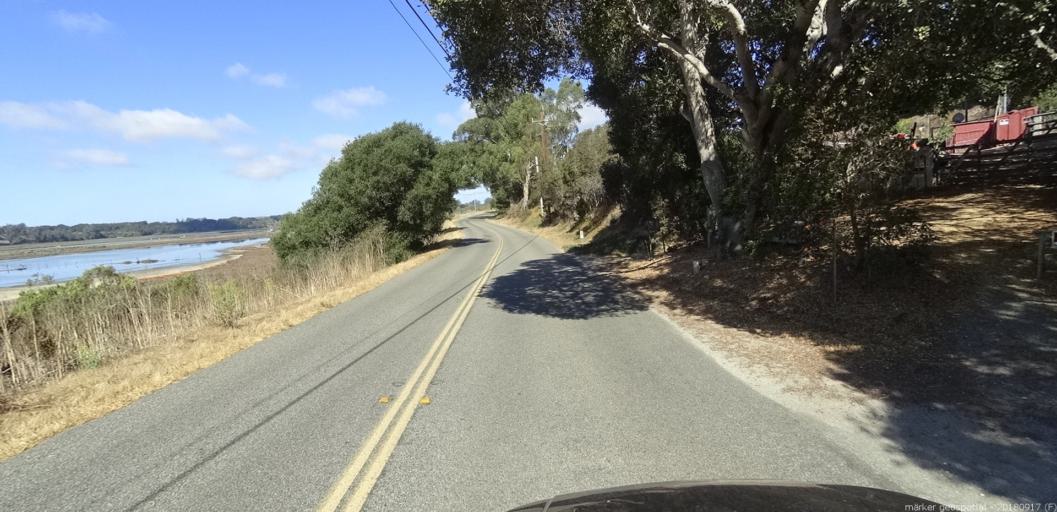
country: US
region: California
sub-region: Monterey County
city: Elkhorn
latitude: 36.8404
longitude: -121.7369
